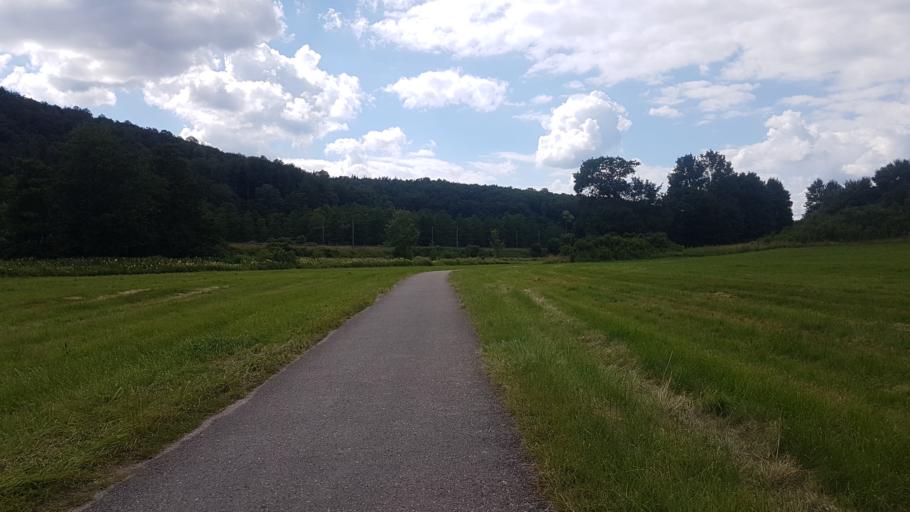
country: DE
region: Bavaria
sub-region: Regierungsbezirk Mittelfranken
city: Pappenheim
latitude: 48.9308
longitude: 10.9576
